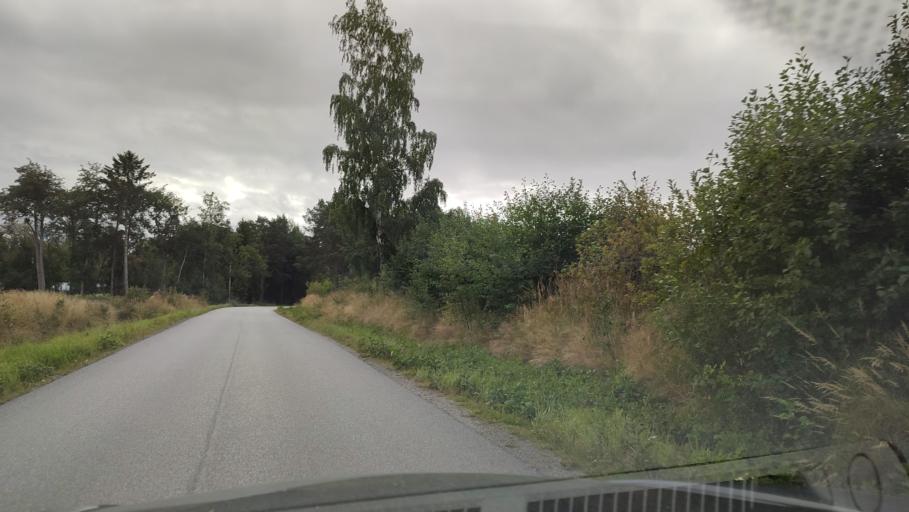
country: FI
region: Ostrobothnia
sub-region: Sydosterbotten
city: Kristinestad
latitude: 62.2601
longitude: 21.3593
